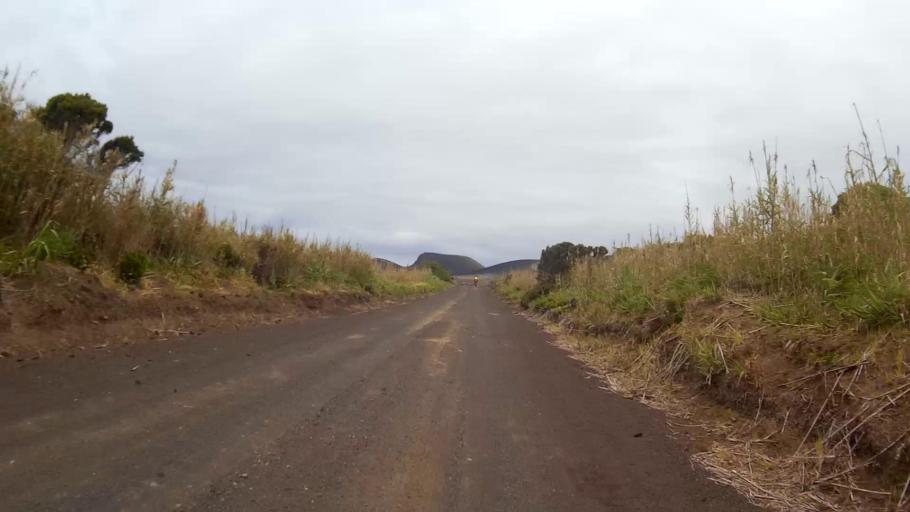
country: PT
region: Azores
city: Ribeira Grande
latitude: 38.5875
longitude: -28.8215
